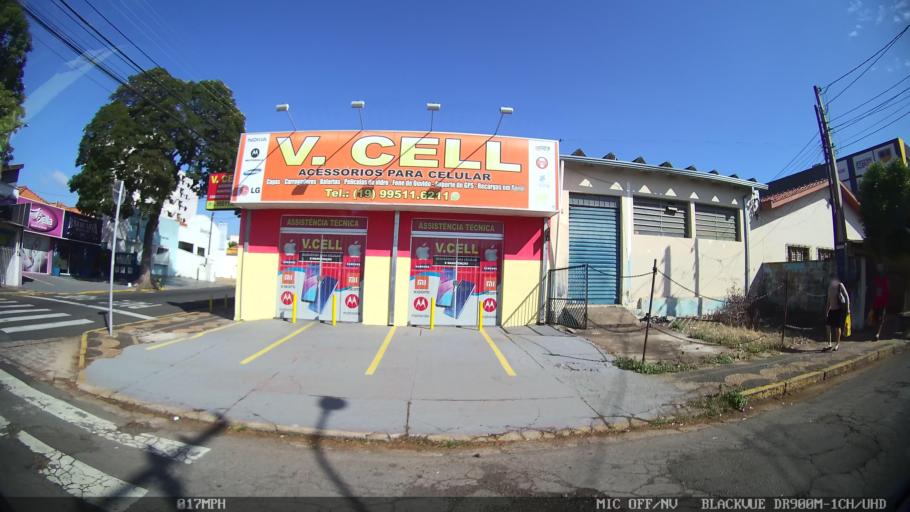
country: BR
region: Sao Paulo
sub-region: Americana
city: Americana
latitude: -22.7491
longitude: -47.3277
